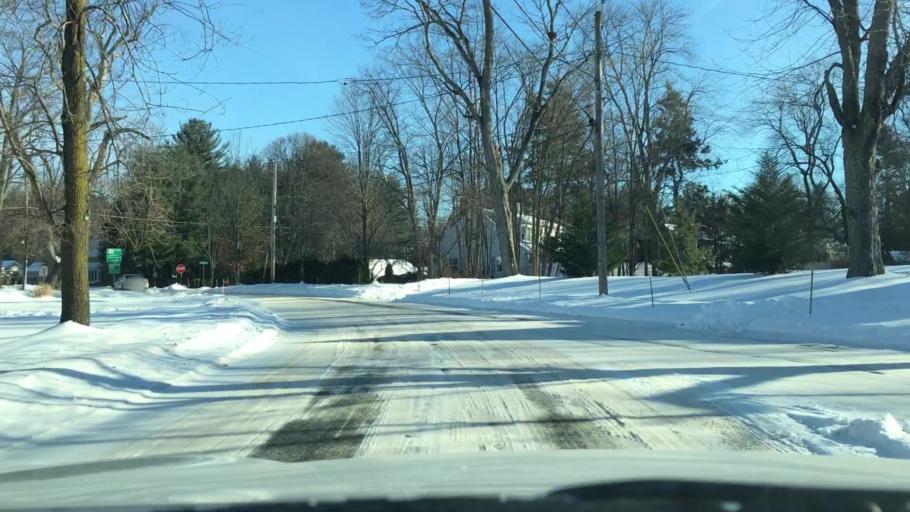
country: US
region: Massachusetts
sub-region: Hampden County
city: Longmeadow
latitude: 42.0488
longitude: -72.5744
